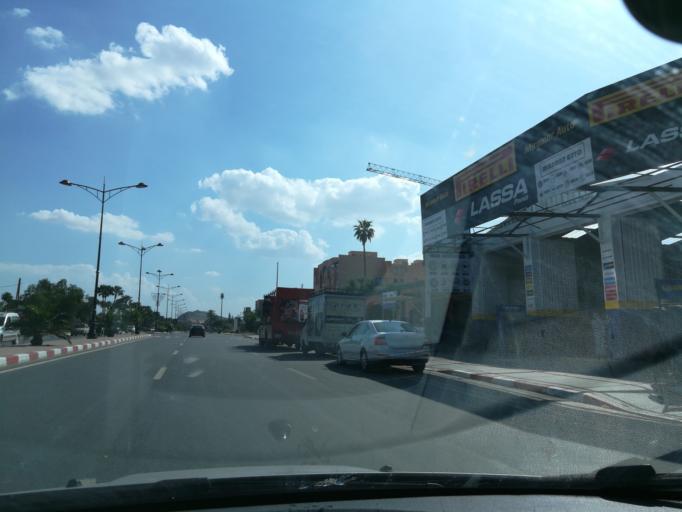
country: MA
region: Marrakech-Tensift-Al Haouz
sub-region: Marrakech
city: Marrakesh
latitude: 31.6625
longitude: -8.0144
